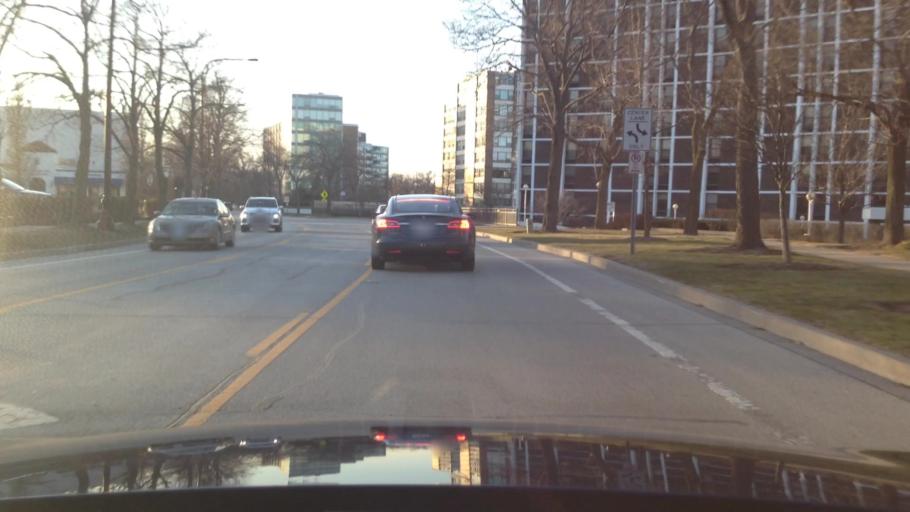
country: US
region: Illinois
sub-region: Cook County
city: Kenilworth
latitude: 42.0866
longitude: -87.6998
